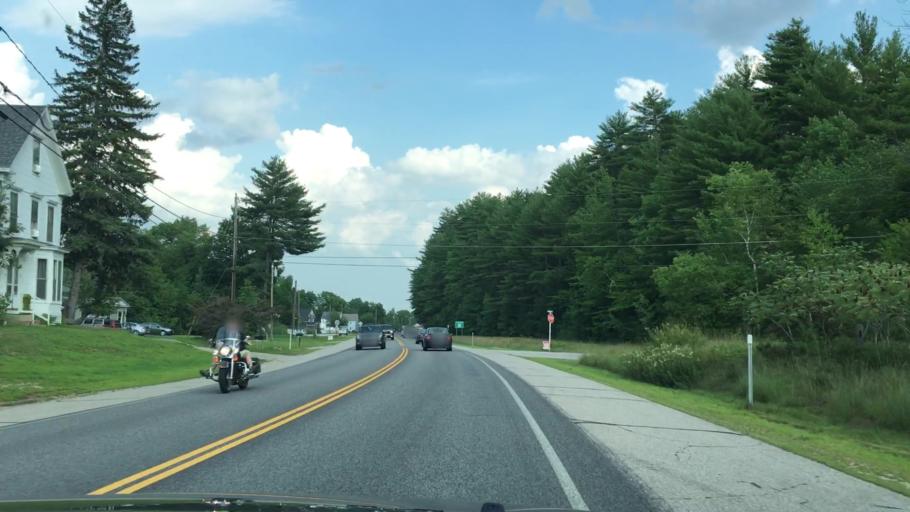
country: US
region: New Hampshire
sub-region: Strafford County
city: Farmington
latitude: 43.3863
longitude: -71.0803
